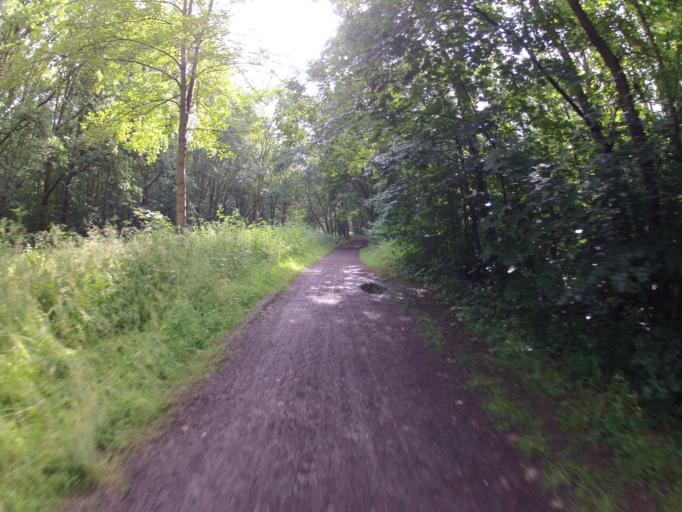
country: DE
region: Saxony
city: Markkleeberg
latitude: 51.3001
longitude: 12.3468
